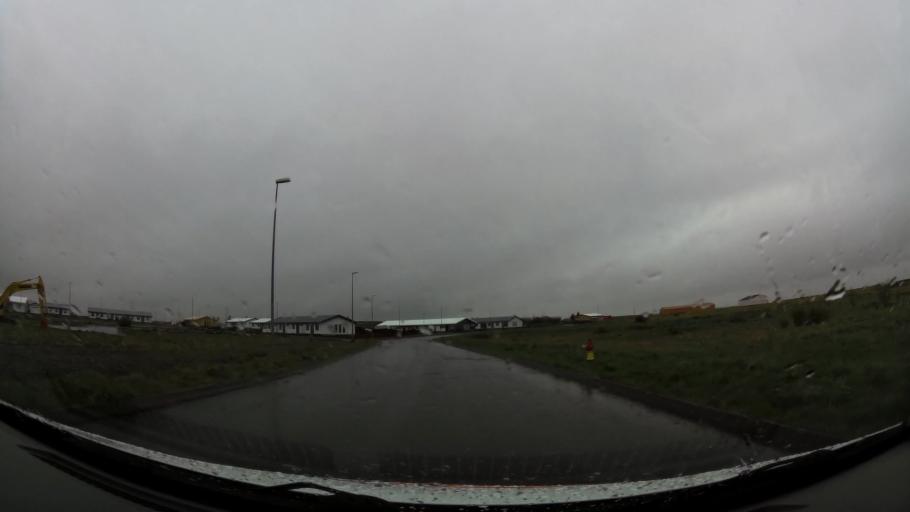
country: IS
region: South
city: Selfoss
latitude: 63.9306
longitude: -21.0274
